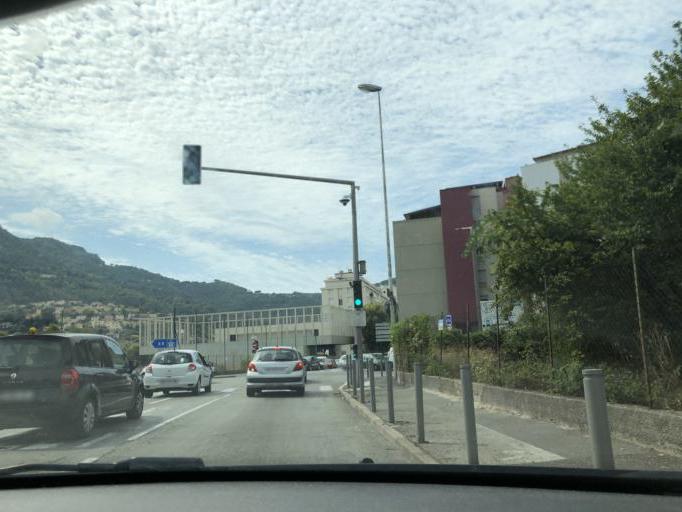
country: FR
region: Provence-Alpes-Cote d'Azur
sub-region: Departement des Alpes-Maritimes
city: La Trinite
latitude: 43.7414
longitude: 7.3089
